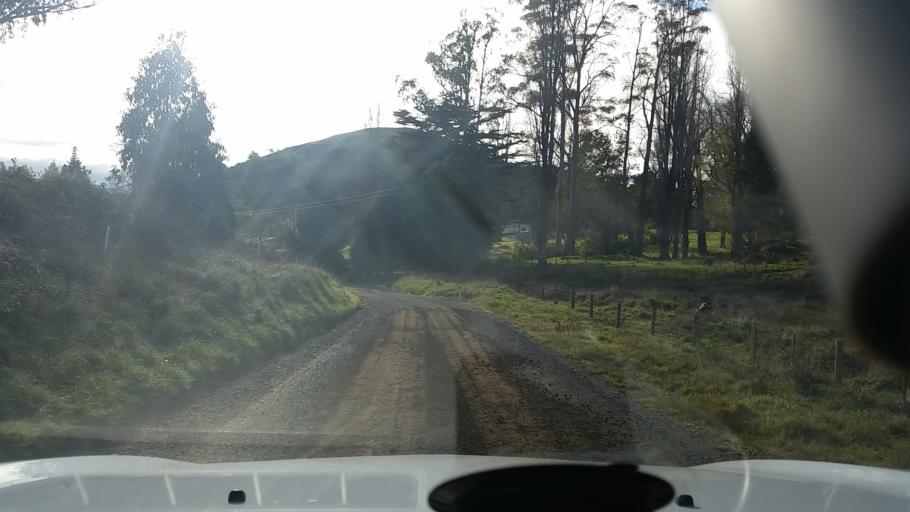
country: NZ
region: Hawke's Bay
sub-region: Napier City
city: Napier
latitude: -39.2416
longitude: 176.8151
